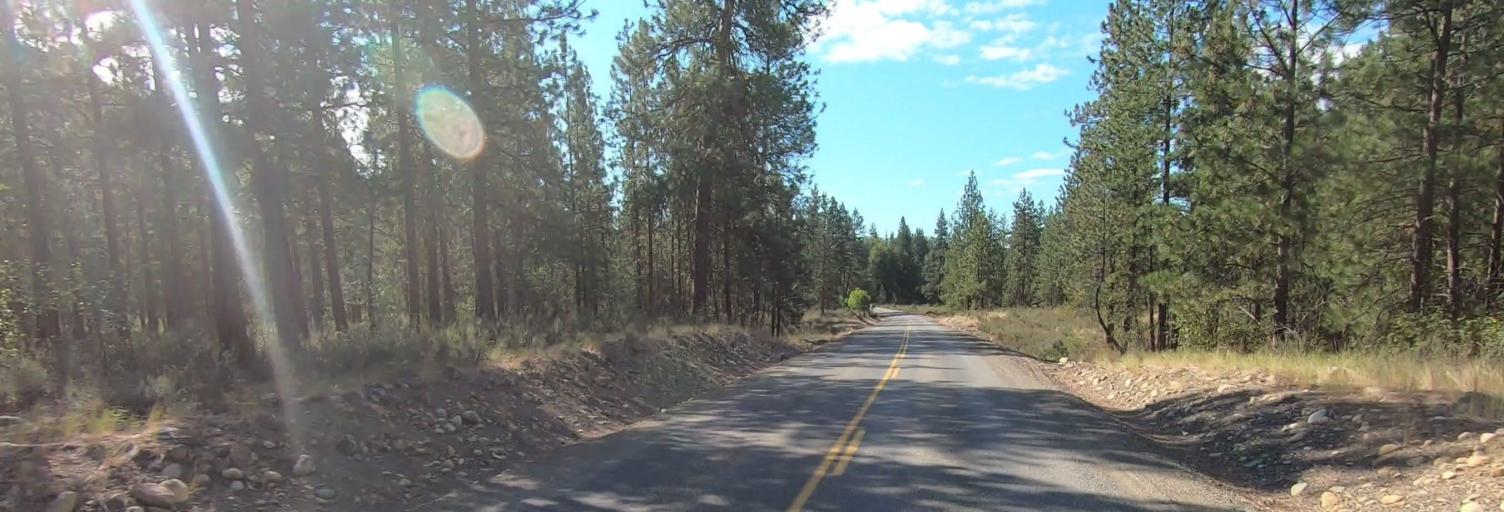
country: US
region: Washington
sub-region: Okanogan County
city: Brewster
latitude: 48.5337
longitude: -120.1788
